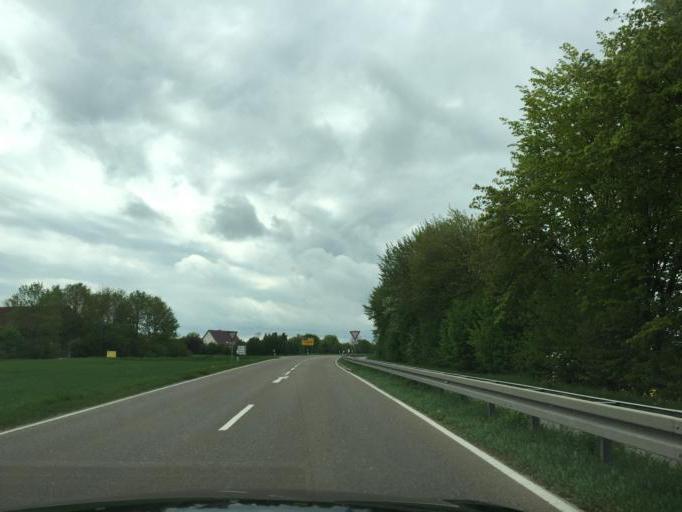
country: DE
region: Bavaria
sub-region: Swabia
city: Dillingen an der Donau
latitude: 48.5604
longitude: 10.5163
